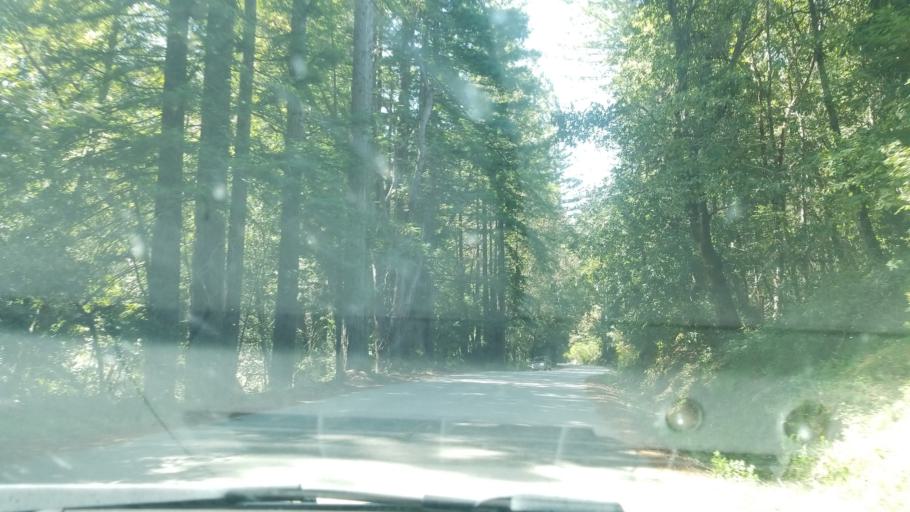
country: US
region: California
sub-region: Santa Cruz County
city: Day Valley
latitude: 37.0784
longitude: -121.8452
